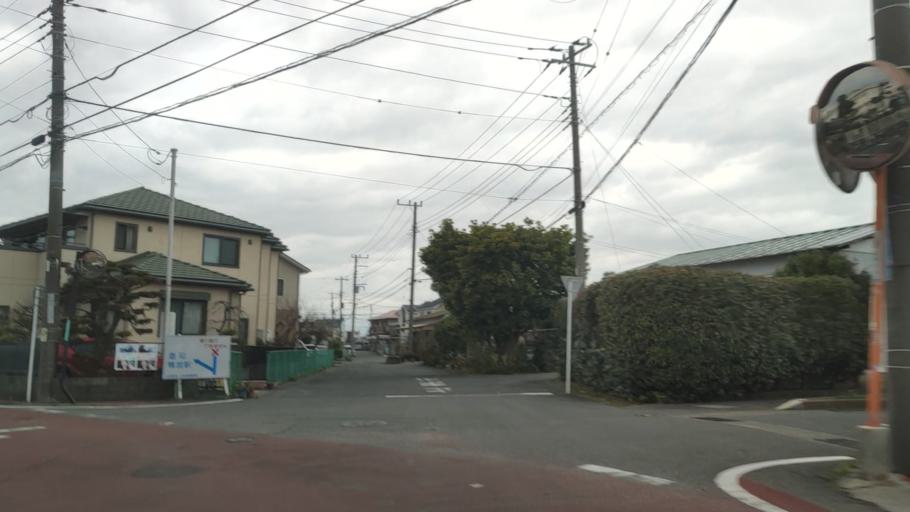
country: JP
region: Kanagawa
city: Odawara
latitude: 35.2755
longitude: 139.1876
